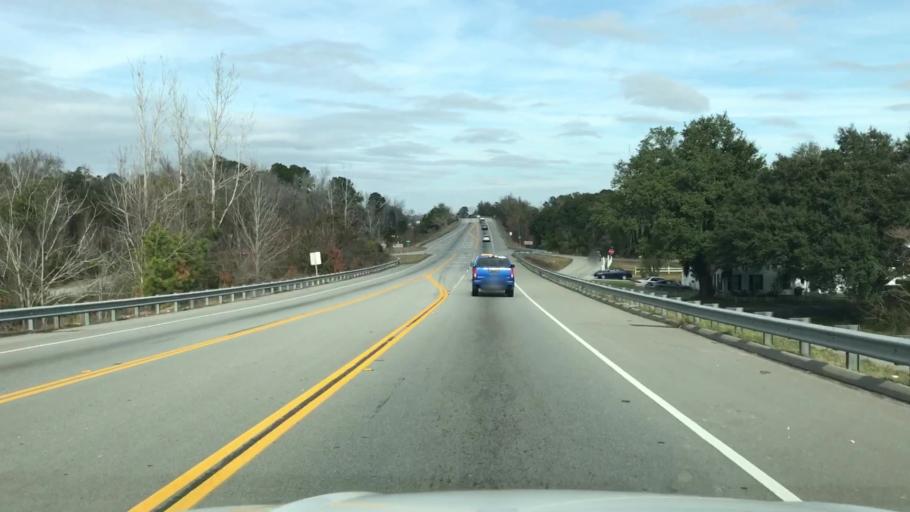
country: US
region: South Carolina
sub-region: Charleston County
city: Shell Point
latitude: 32.7892
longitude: -80.1080
